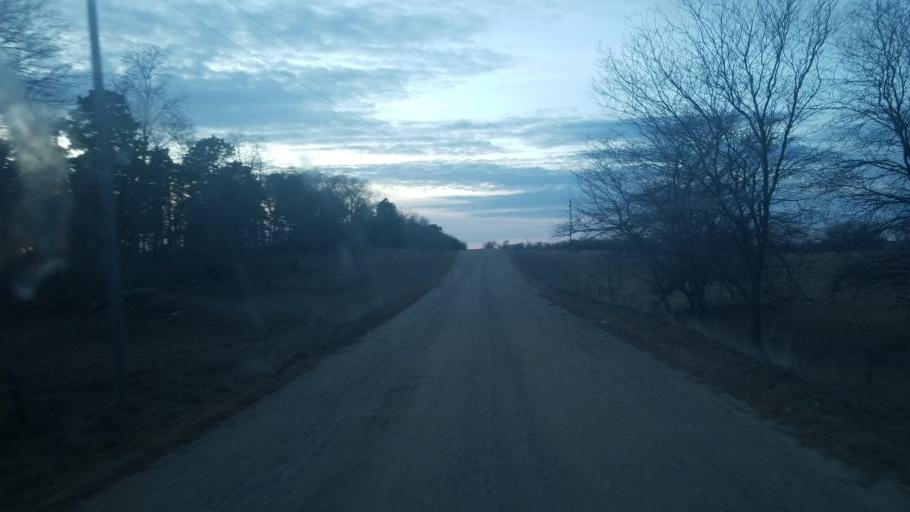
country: US
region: Nebraska
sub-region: Knox County
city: Center
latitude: 42.6554
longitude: -97.7706
